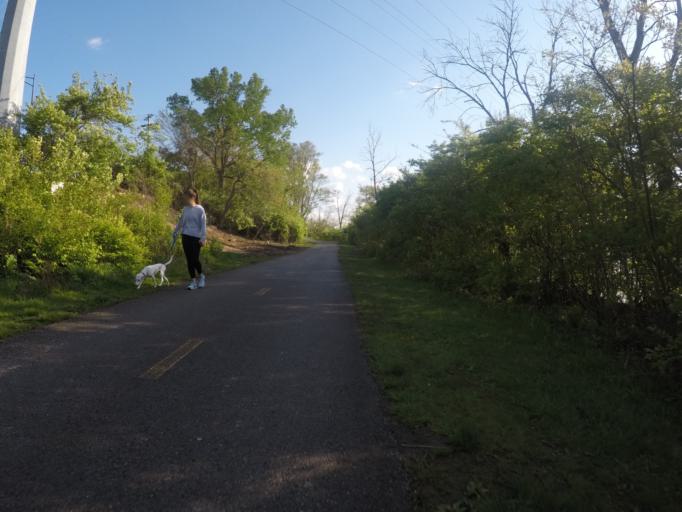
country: US
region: Ohio
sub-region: Franklin County
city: Columbus
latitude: 39.9516
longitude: -83.0117
